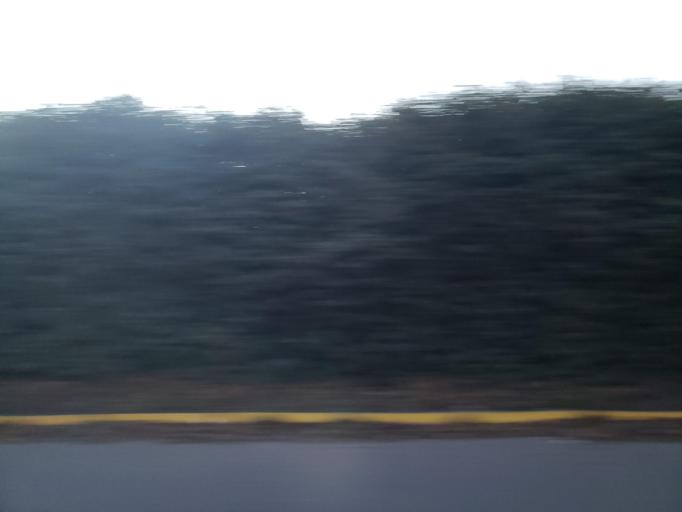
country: CL
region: Santiago Metropolitan
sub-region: Provincia de Talagante
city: El Monte
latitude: -33.6855
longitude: -70.9680
